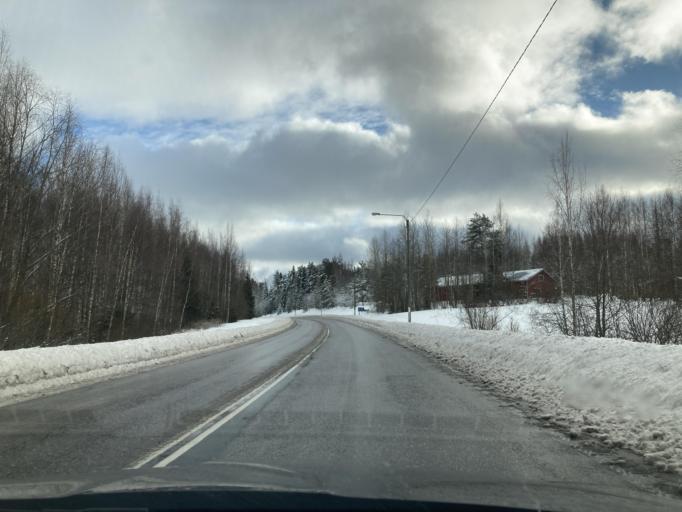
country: FI
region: Central Finland
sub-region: Jaemsae
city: Jaemsae
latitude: 61.8076
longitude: 25.1812
